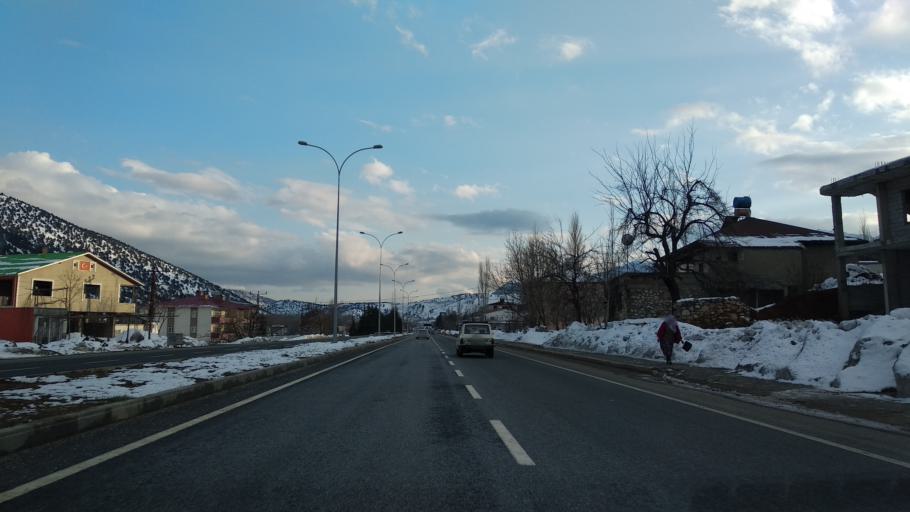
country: TR
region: Kahramanmaras
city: Goksun
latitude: 37.8923
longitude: 36.6210
